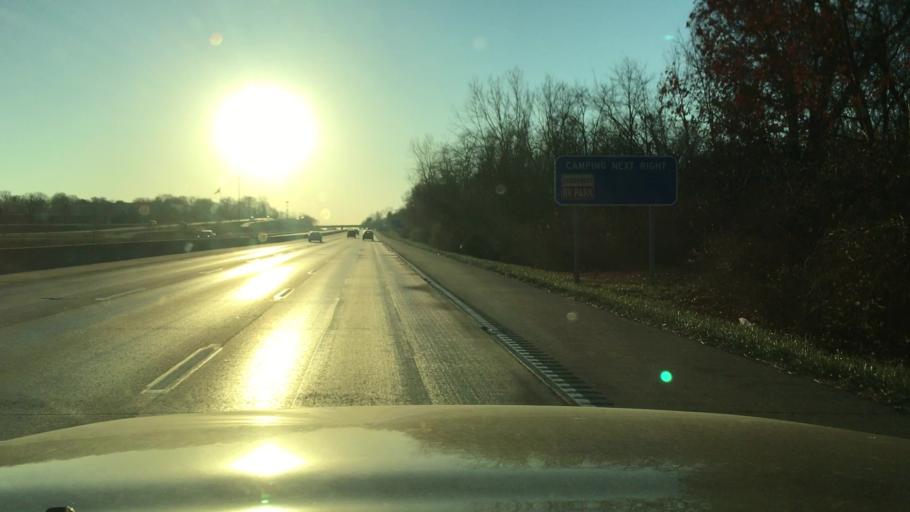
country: US
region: Missouri
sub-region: Saint Charles County
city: Saint Charles
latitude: 38.8131
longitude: -90.4905
